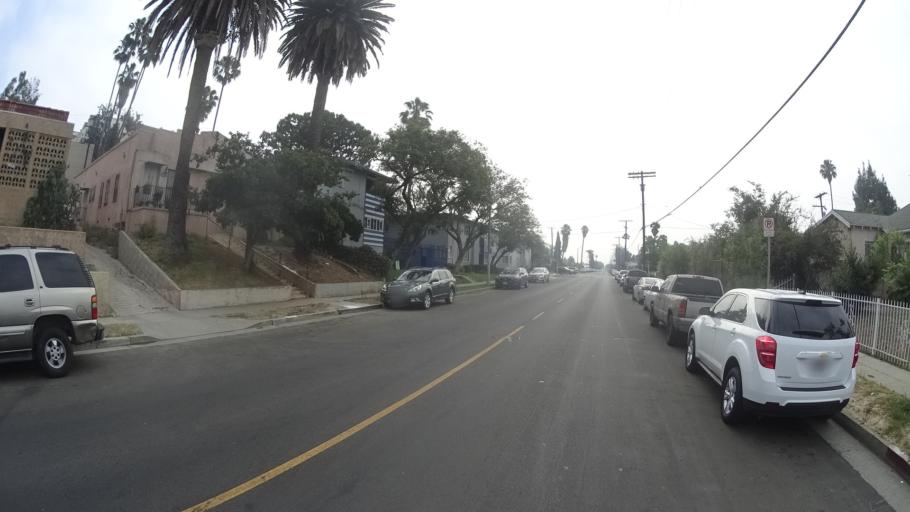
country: US
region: California
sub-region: Los Angeles County
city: View Park-Windsor Hills
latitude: 34.0296
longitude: -118.3259
